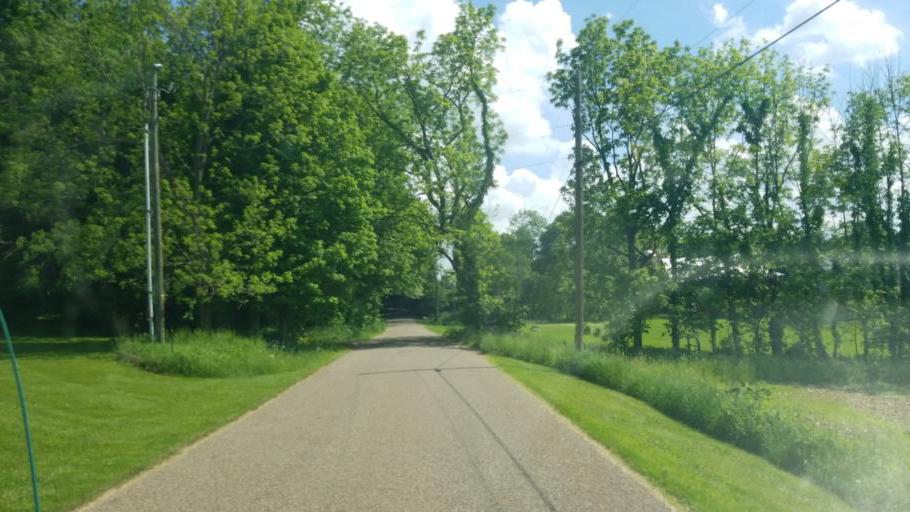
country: US
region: Ohio
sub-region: Sandusky County
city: Bellville
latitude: 40.6502
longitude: -82.5260
